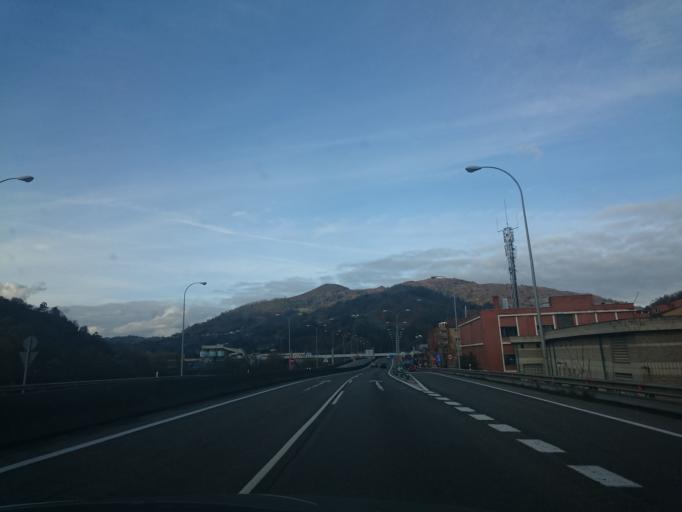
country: ES
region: Asturias
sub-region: Province of Asturias
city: Mieres
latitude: 43.2523
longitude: -5.7811
